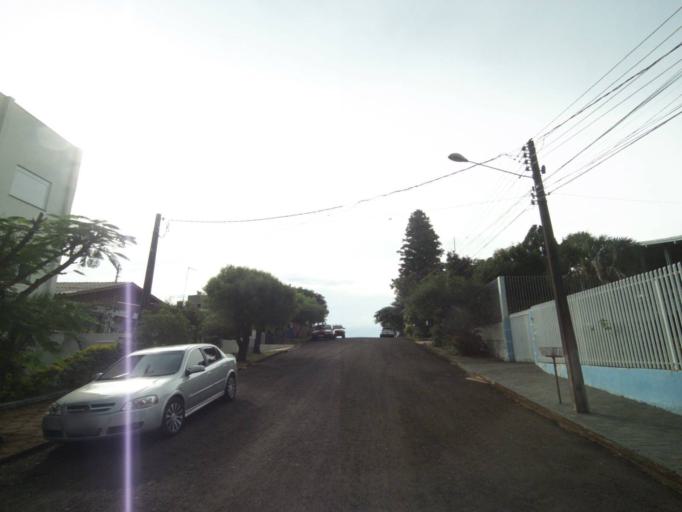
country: BR
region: Parana
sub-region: Guaraniacu
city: Guaraniacu
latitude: -25.1009
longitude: -52.8711
